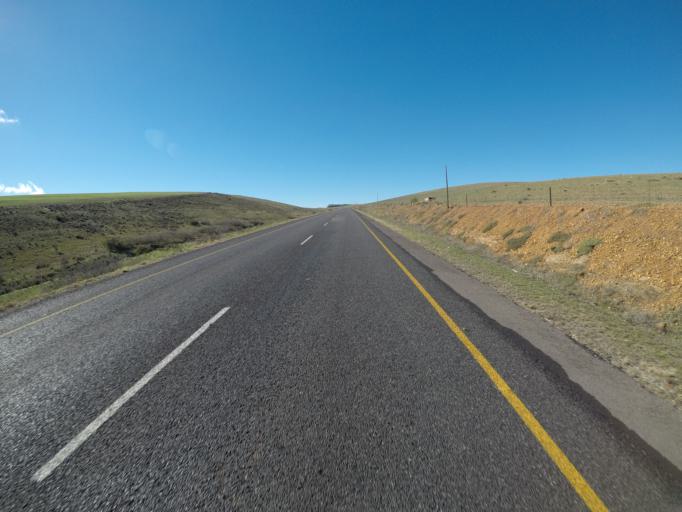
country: ZA
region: Western Cape
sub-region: Overberg District Municipality
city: Caledon
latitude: -34.1475
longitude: 19.4882
